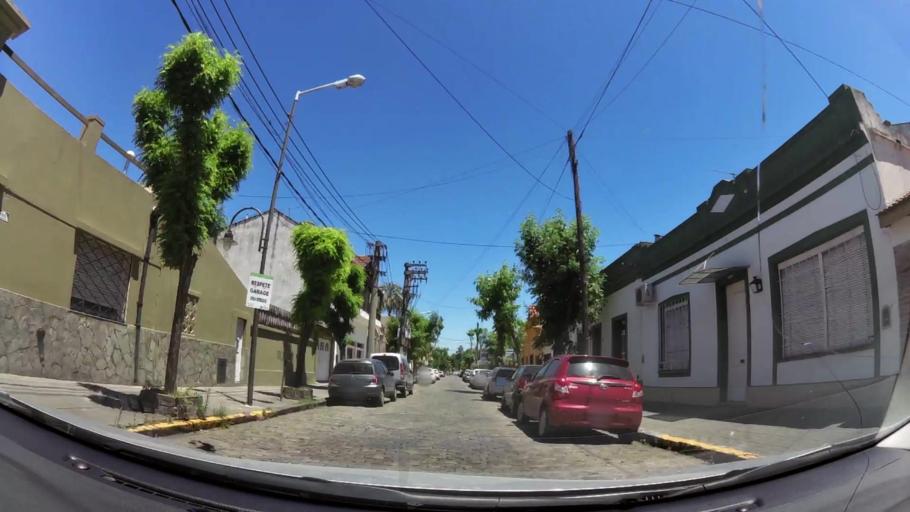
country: AR
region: Buenos Aires
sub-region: Partido de Tigre
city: Tigre
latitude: -34.4450
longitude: -58.5535
